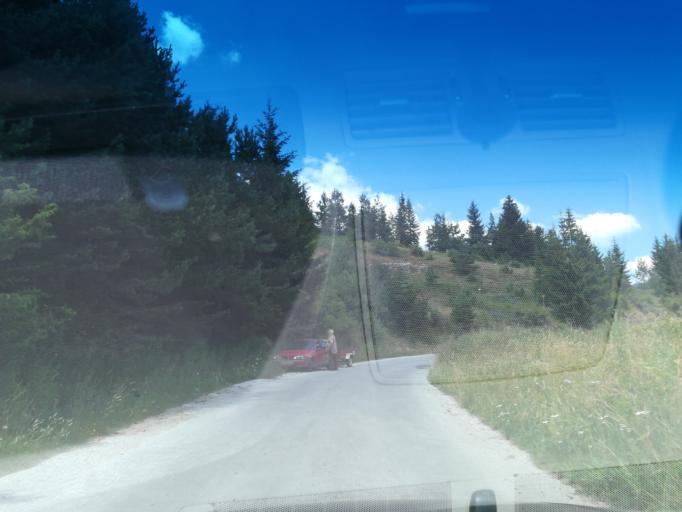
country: BG
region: Smolyan
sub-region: Obshtina Chepelare
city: Chepelare
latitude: 41.6753
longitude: 24.7746
